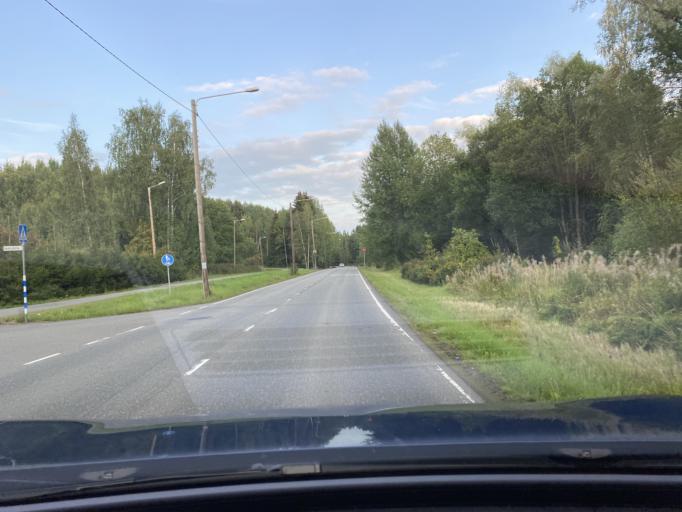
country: FI
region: Kymenlaakso
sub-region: Kouvola
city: Kouvola
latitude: 60.8969
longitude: 26.6597
